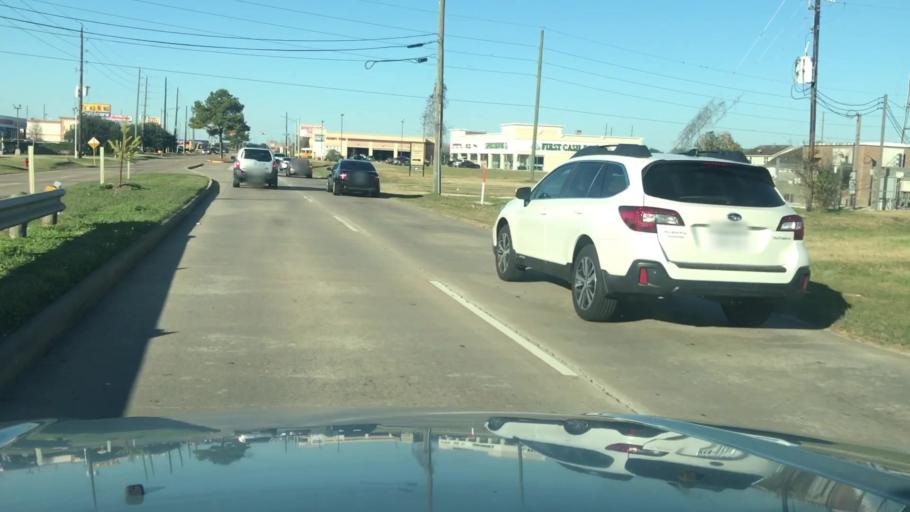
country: US
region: Texas
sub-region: Harris County
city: Oak Cliff Place
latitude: 29.8530
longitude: -95.7186
